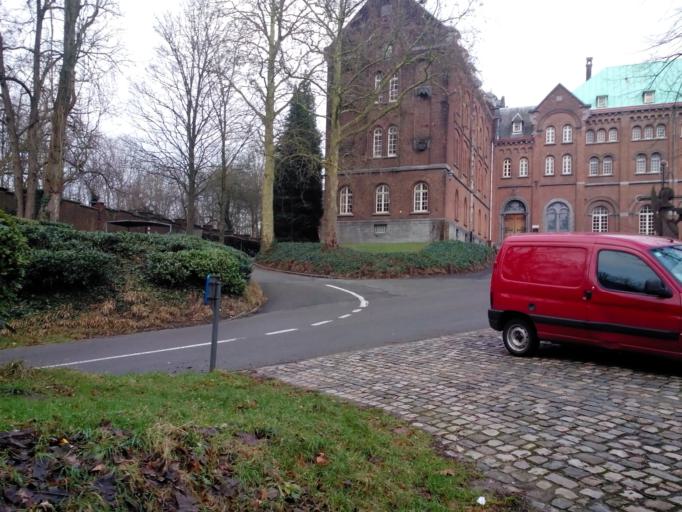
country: BE
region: Flanders
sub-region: Provincie Vlaams-Brabant
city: Leuven
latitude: 50.8887
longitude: 4.6953
